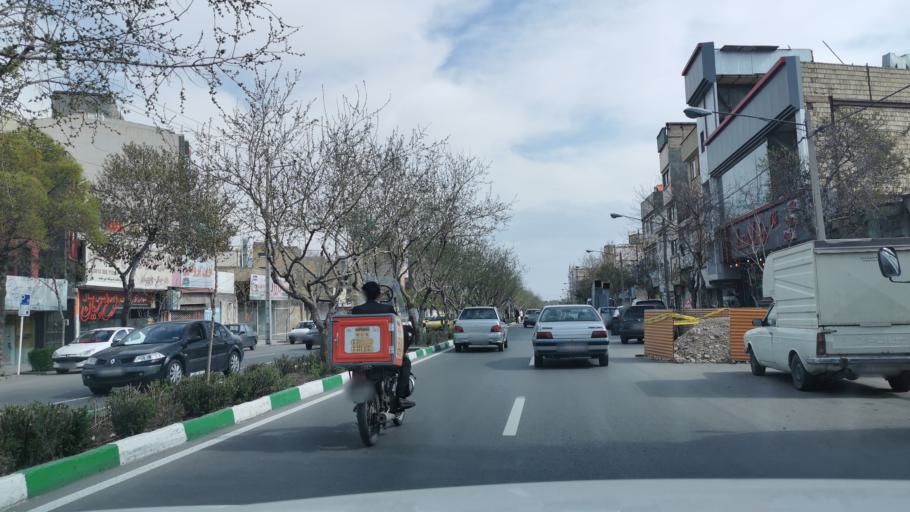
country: IR
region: Razavi Khorasan
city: Mashhad
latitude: 36.3145
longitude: 59.6112
